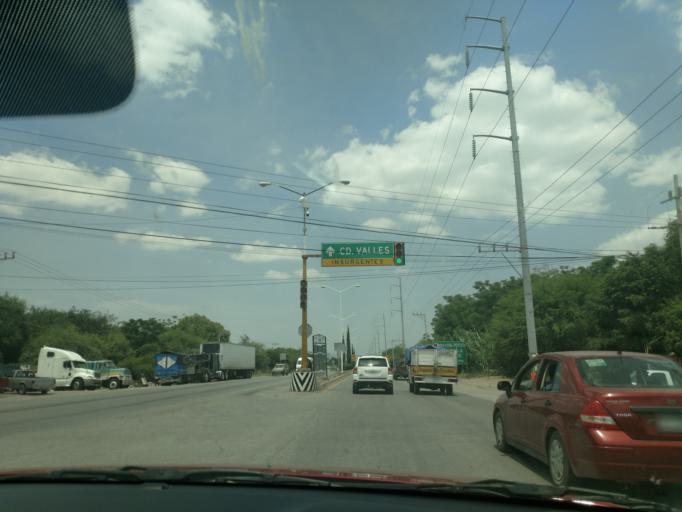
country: MX
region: San Luis Potosi
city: Rio Verde
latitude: 21.9224
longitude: -99.9809
